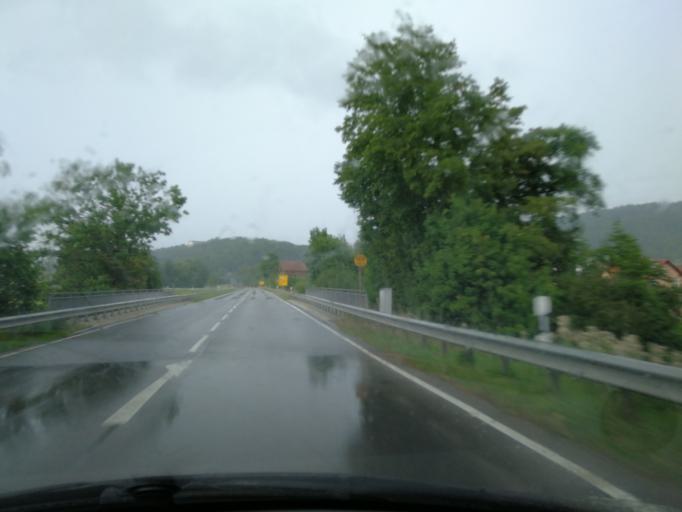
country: DE
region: Bavaria
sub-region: Upper Palatinate
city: Donaustauf
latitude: 49.0267
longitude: 12.2393
